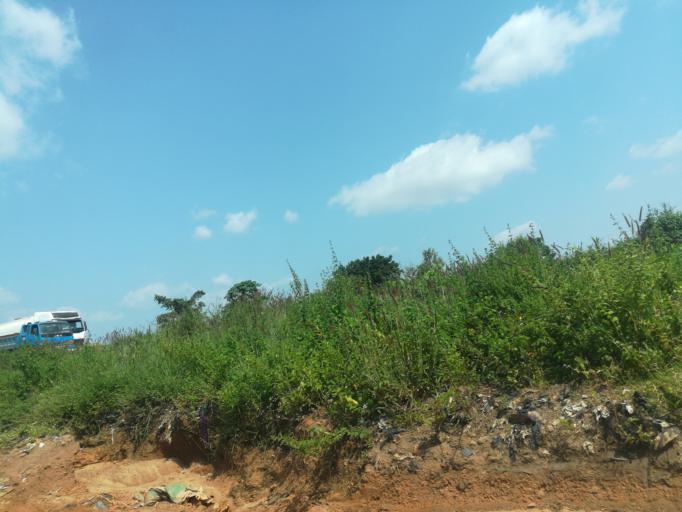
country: NG
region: Oyo
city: Moniya
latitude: 7.5064
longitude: 3.9161
